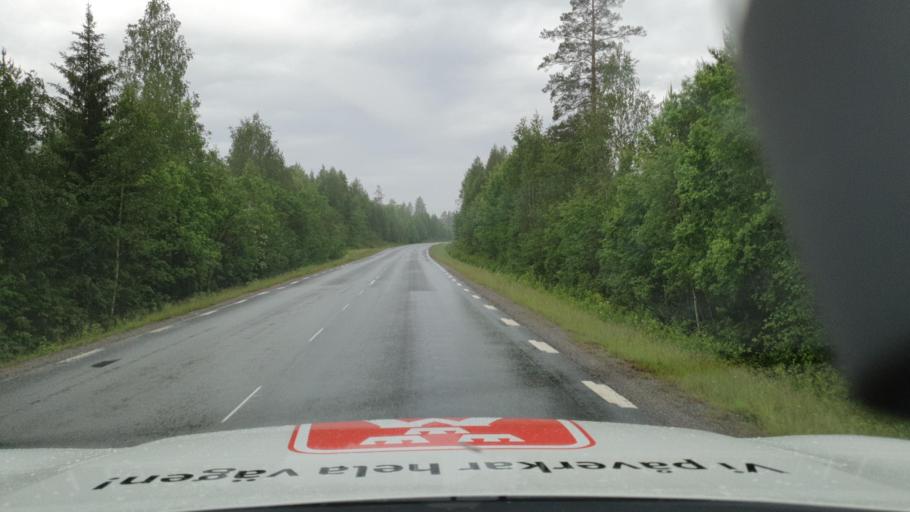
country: SE
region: Vaesterbotten
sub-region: Vannas Kommun
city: Vaennaes
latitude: 63.7823
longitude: 19.7391
